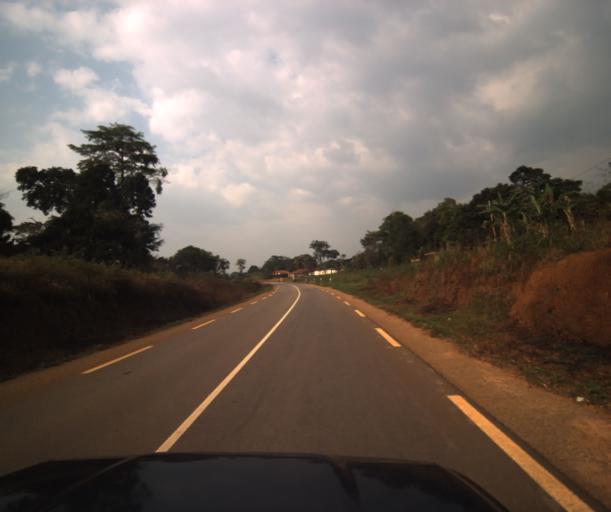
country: CM
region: Centre
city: Mbankomo
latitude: 3.7168
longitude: 11.3811
